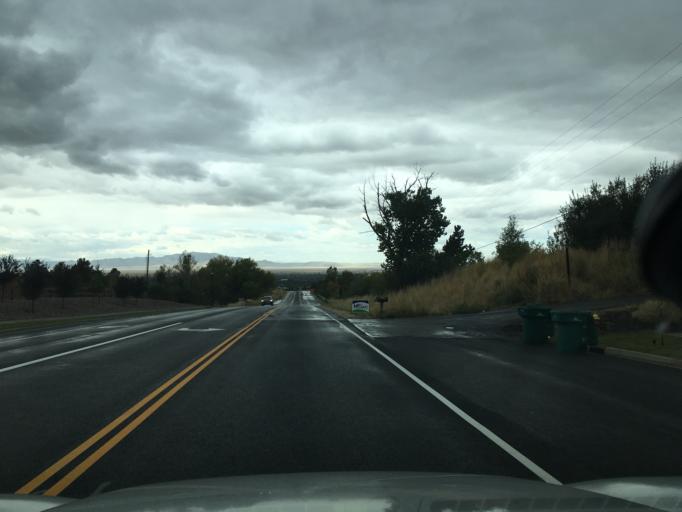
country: US
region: Utah
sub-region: Davis County
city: Kaysville
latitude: 41.0655
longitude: -111.9187
